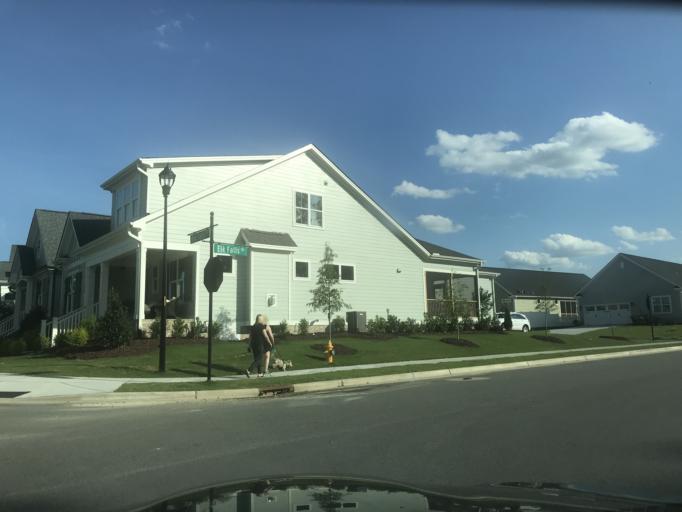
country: US
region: North Carolina
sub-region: Wake County
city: Knightdale
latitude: 35.7652
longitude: -78.4267
